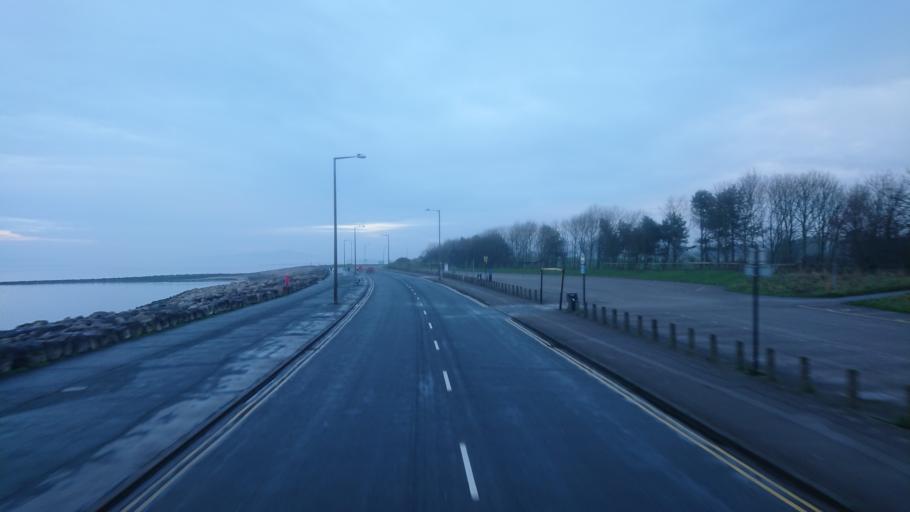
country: GB
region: England
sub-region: Lancashire
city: Morecambe
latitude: 54.0821
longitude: -2.8352
